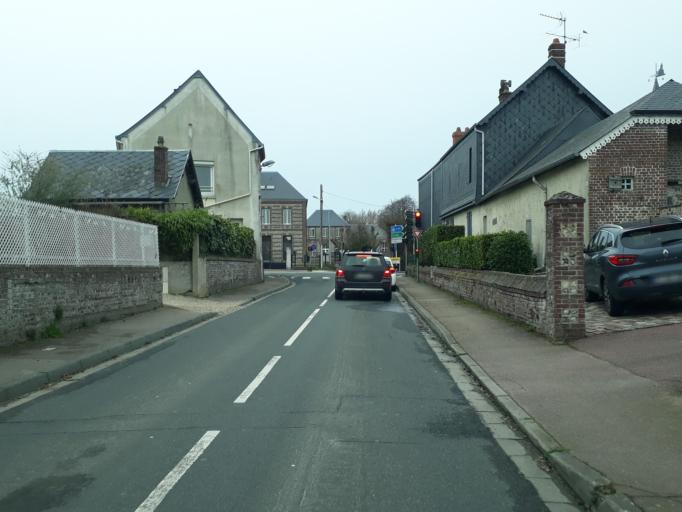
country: FR
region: Haute-Normandie
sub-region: Departement de la Seine-Maritime
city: Goderville
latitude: 49.6445
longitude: 0.3645
